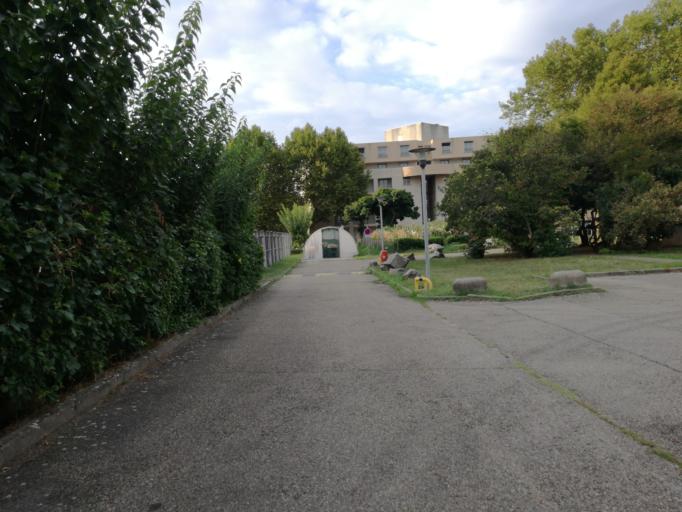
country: FR
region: Rhone-Alpes
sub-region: Departement du Rhone
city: La Mulatiere
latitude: 45.7305
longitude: 4.8259
